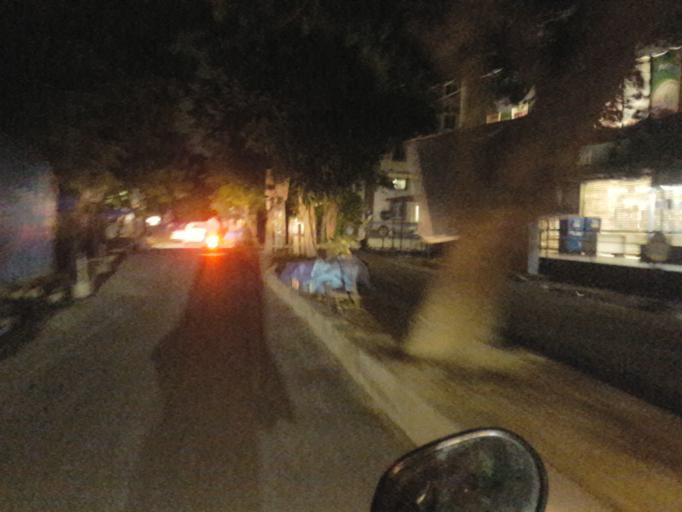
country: IN
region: Telangana
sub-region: Rangareddi
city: Kukatpalli
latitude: 17.4818
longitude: 78.3915
